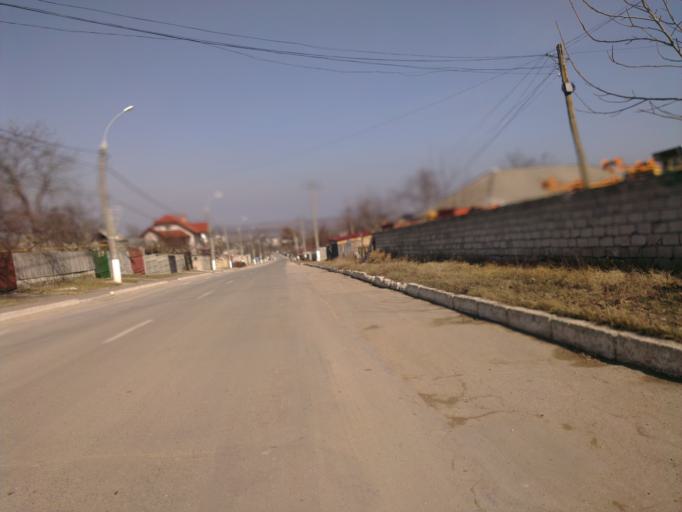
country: MD
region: Chisinau
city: Cricova
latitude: 47.1315
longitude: 28.8656
